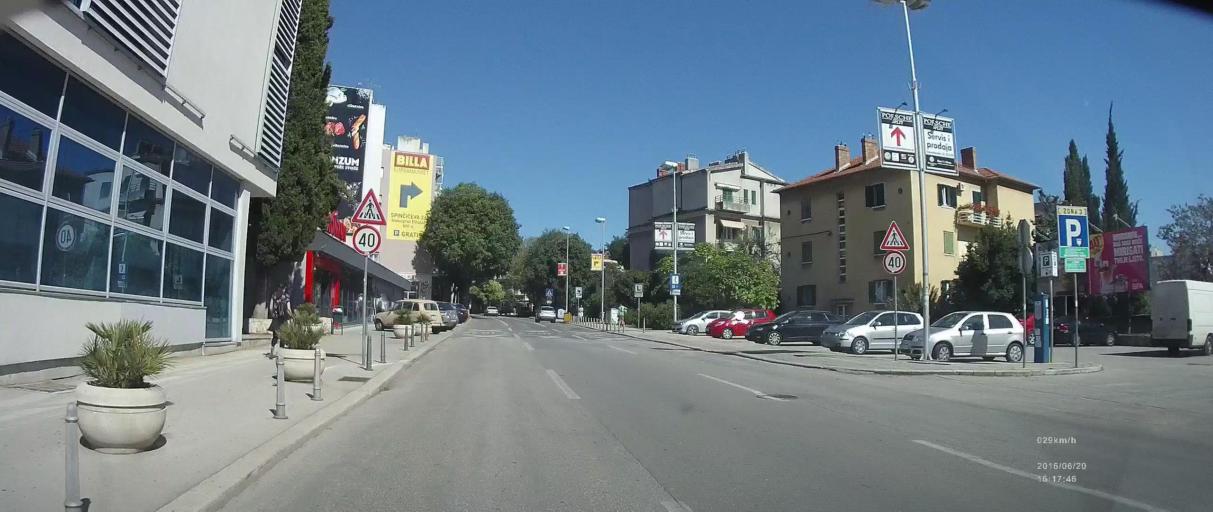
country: HR
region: Splitsko-Dalmatinska
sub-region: Grad Split
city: Split
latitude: 43.5053
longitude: 16.4484
